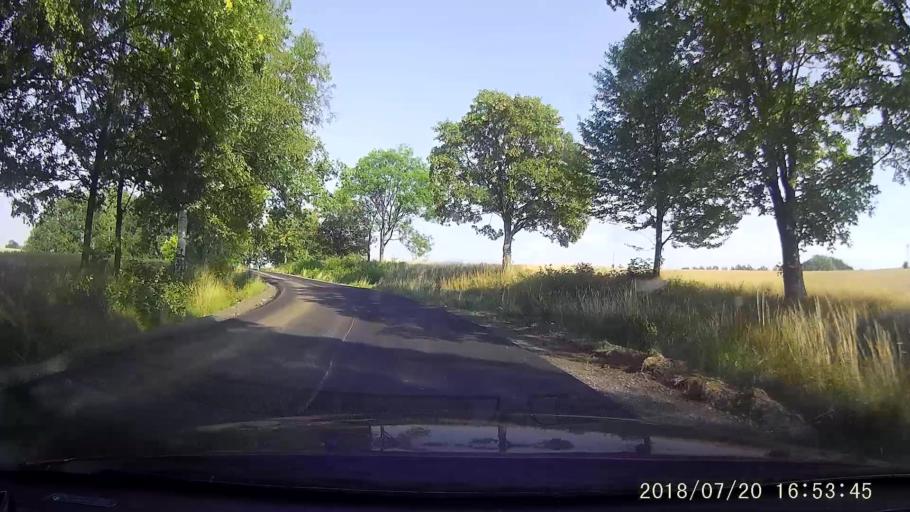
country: PL
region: Lower Silesian Voivodeship
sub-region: Powiat lubanski
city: Lesna
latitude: 51.0350
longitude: 15.2439
